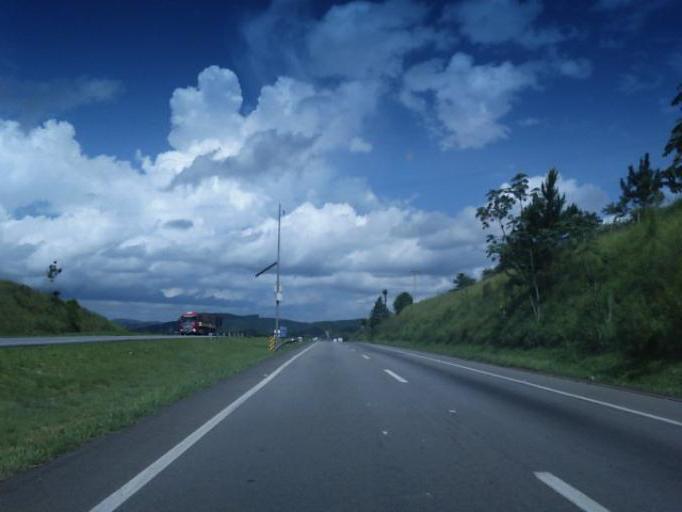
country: BR
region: Sao Paulo
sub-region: Cajati
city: Cajati
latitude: -24.7221
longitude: -48.0661
